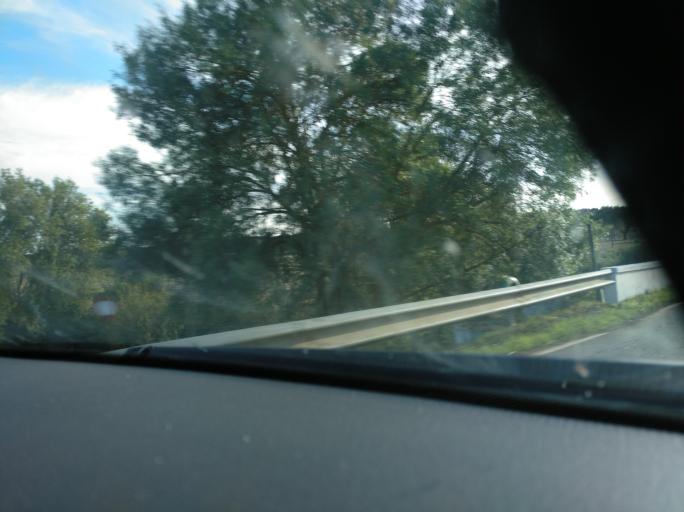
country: PT
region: Portalegre
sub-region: Fronteira
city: Fronteira
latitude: 38.9602
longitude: -7.6115
